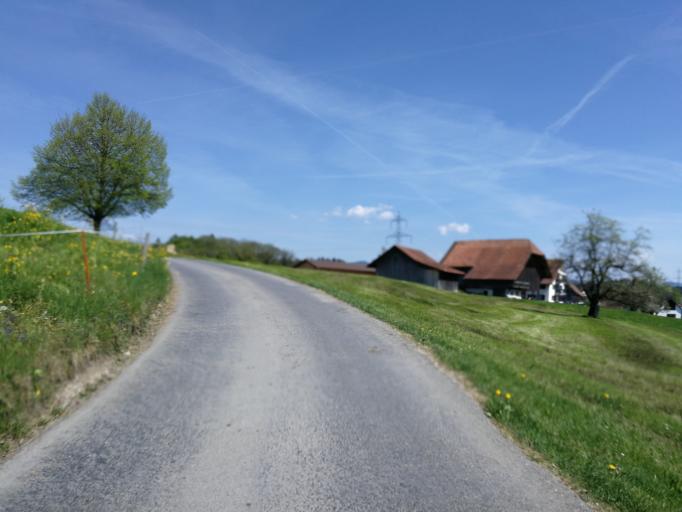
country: CH
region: Zurich
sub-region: Bezirk Meilen
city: Hombrechtikon
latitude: 47.2686
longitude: 8.7718
